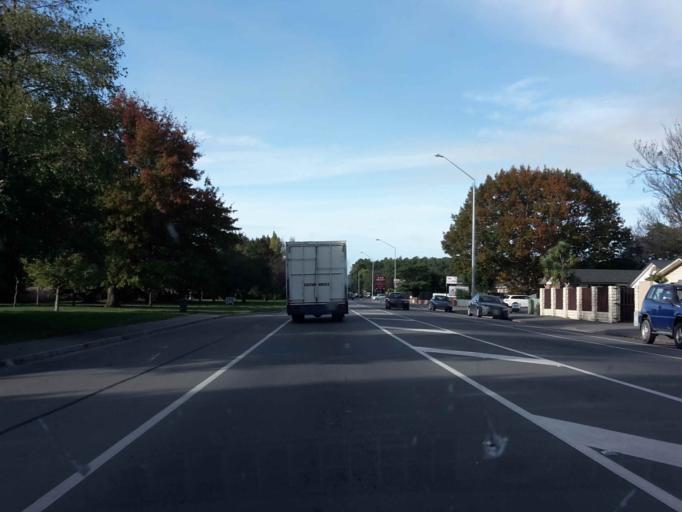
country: NZ
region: Canterbury
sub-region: Ashburton District
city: Tinwald
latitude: -43.9151
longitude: 171.7292
